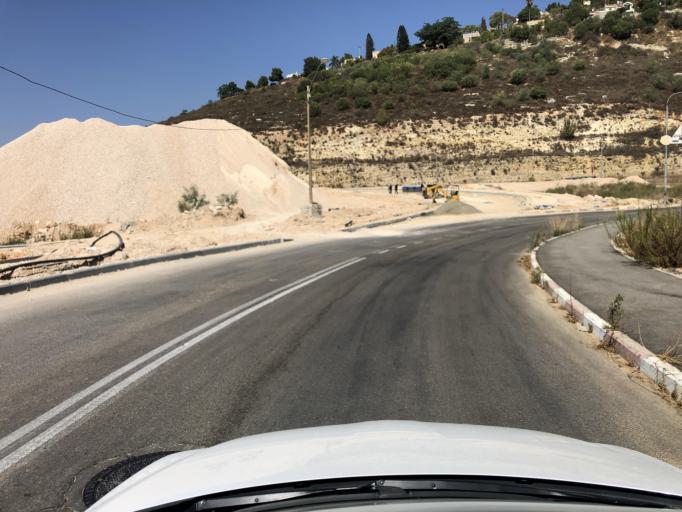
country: PS
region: West Bank
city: An Nabi Ilyas
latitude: 32.1663
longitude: 35.0110
